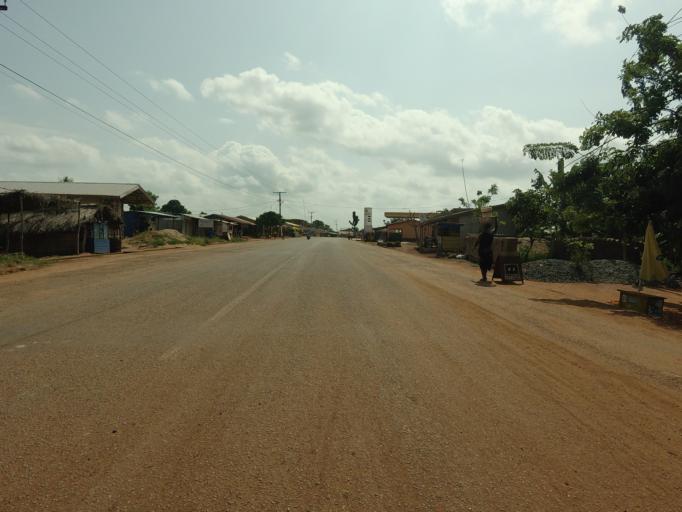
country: TG
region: Maritime
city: Tsevie
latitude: 6.3615
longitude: 0.8606
